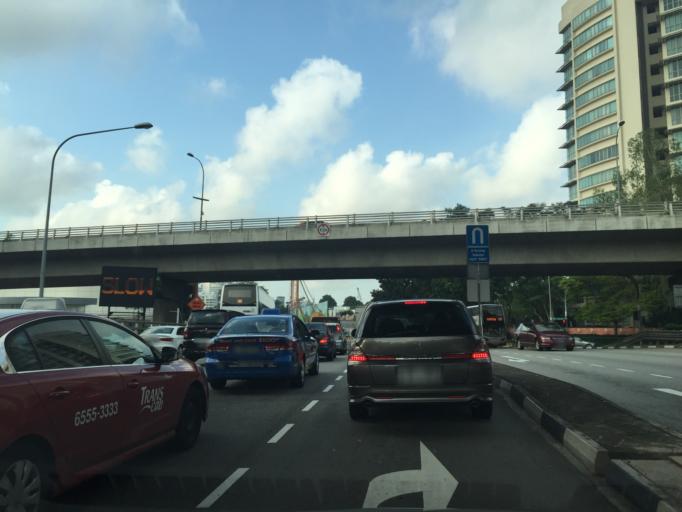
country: SG
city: Singapore
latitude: 1.3210
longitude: 103.8255
